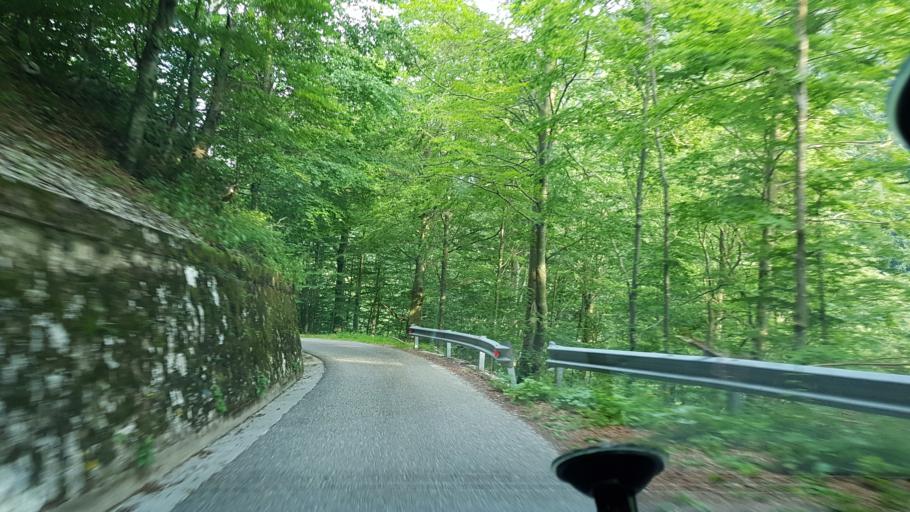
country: IT
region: Friuli Venezia Giulia
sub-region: Provincia di Udine
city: Prato
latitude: 46.3283
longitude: 13.3642
